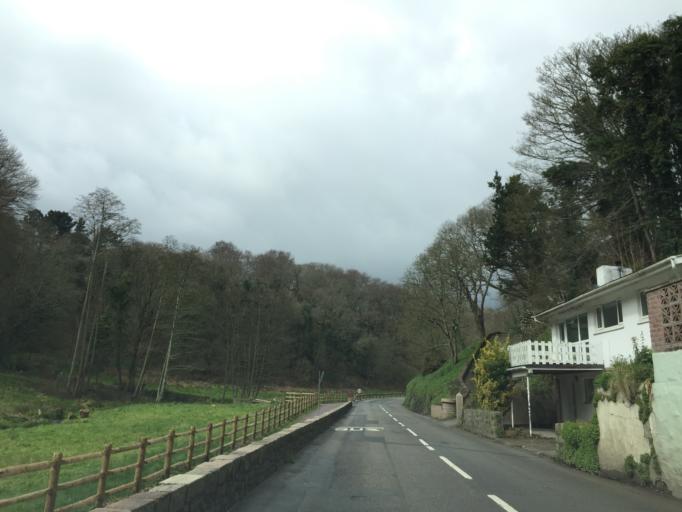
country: JE
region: St Helier
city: Saint Helier
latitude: 49.2127
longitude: -2.1689
